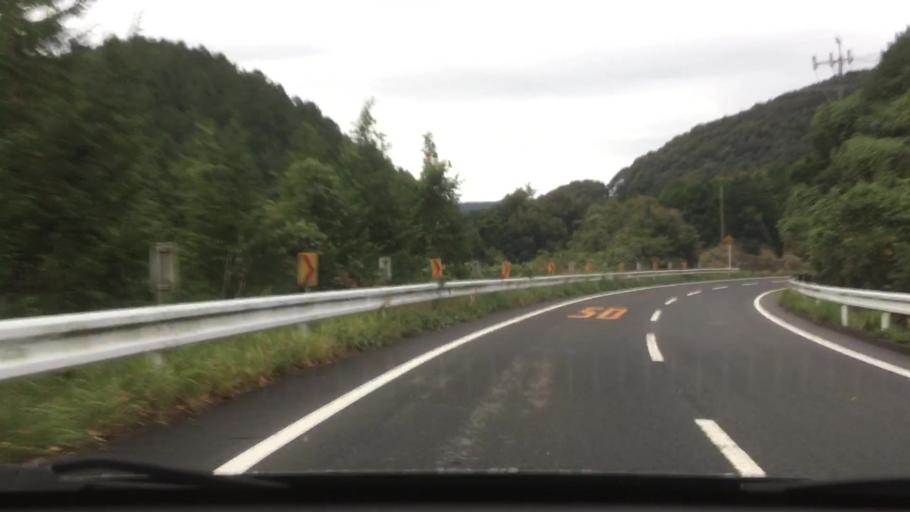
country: JP
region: Nagasaki
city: Sasebo
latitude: 32.9702
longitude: 129.6974
